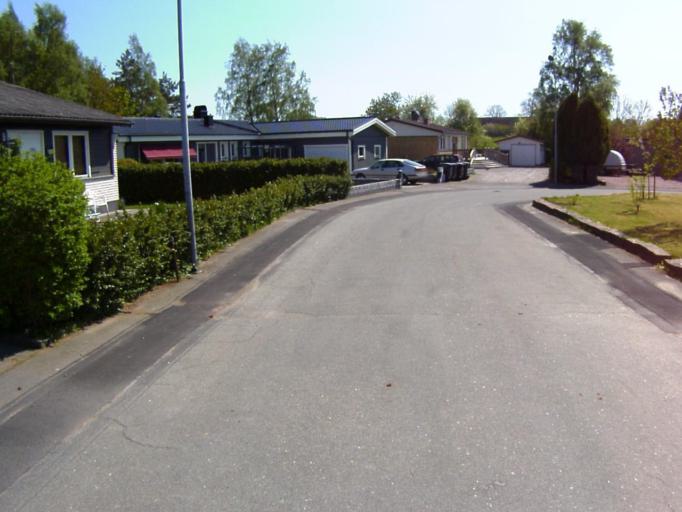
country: SE
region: Skane
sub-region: Kristianstads Kommun
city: Tollarp
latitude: 56.1678
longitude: 14.2954
